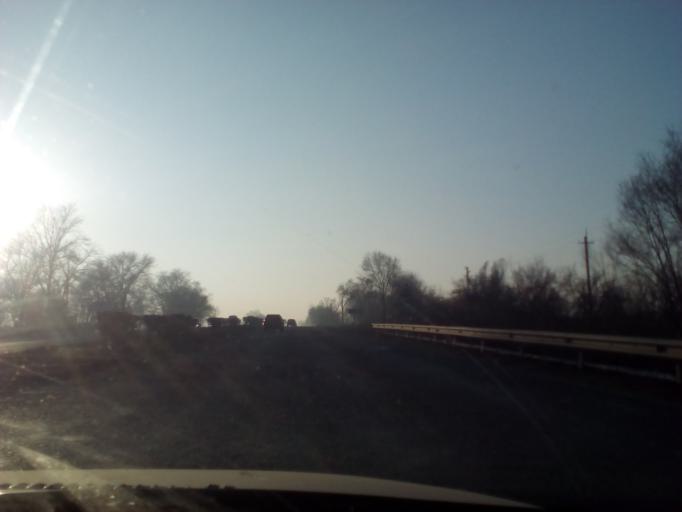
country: KZ
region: Almaty Oblysy
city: Burunday
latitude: 43.2235
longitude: 76.5980
